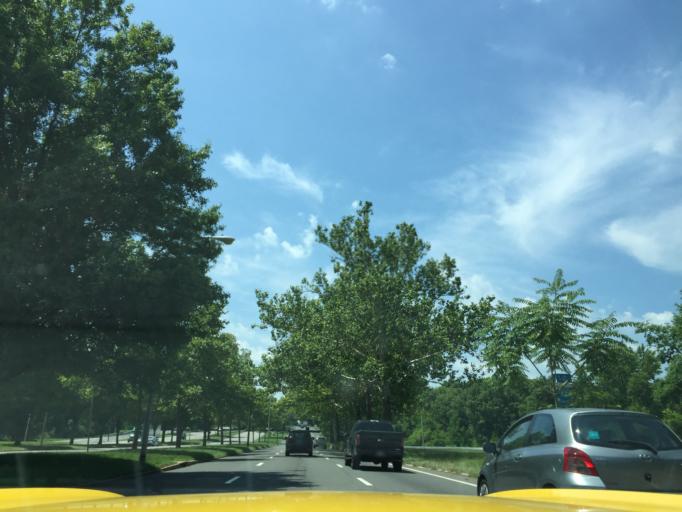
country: US
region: Pennsylvania
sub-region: Bucks County
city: Trevose
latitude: 40.1101
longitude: -74.9942
